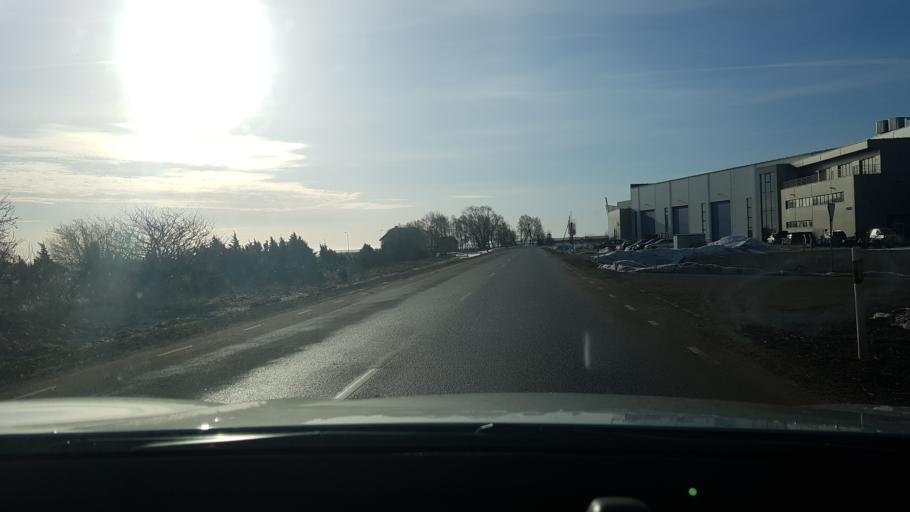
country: EE
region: Saare
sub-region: Kuressaare linn
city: Kuressaare
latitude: 58.2224
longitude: 22.5067
